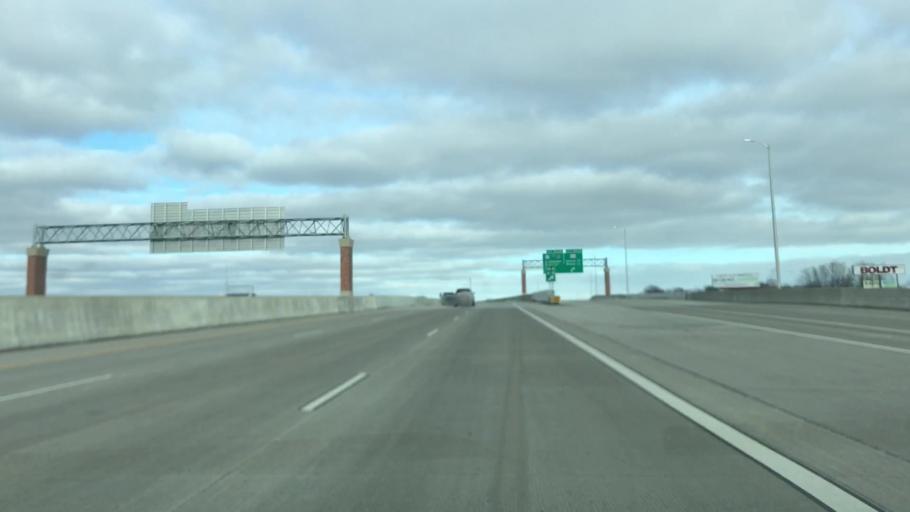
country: US
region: Wisconsin
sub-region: Brown County
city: Ashwaubenon
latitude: 44.4643
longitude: -88.0817
